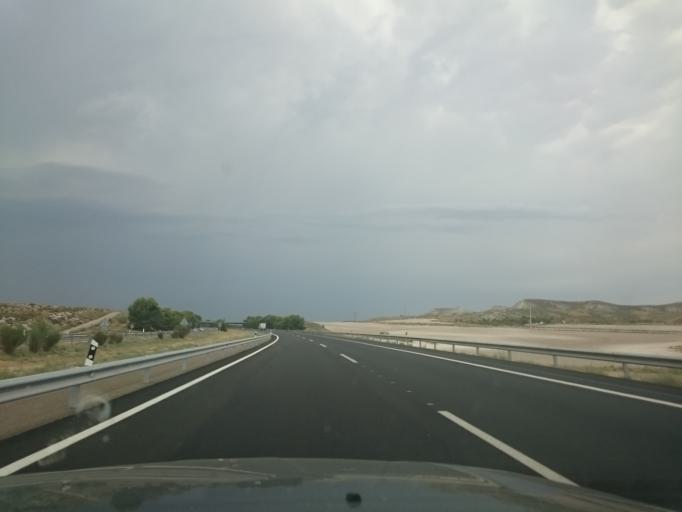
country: ES
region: Aragon
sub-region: Provincia de Zaragoza
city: Pina de Ebro
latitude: 41.5260
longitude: -0.4730
